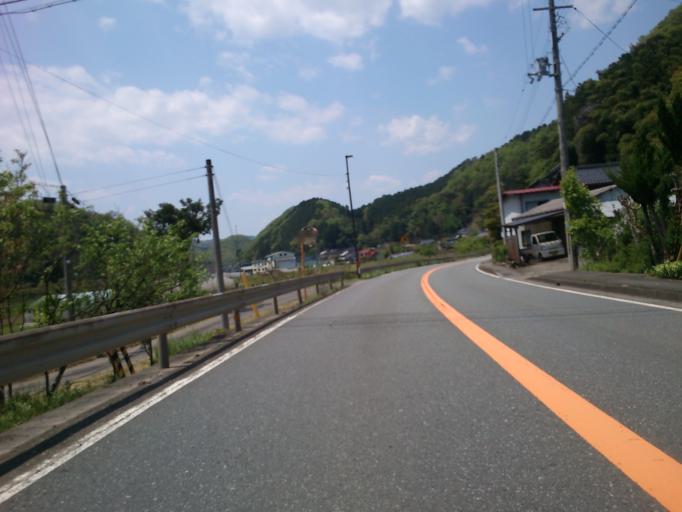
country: JP
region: Kyoto
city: Fukuchiyama
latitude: 35.3244
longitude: 134.9689
